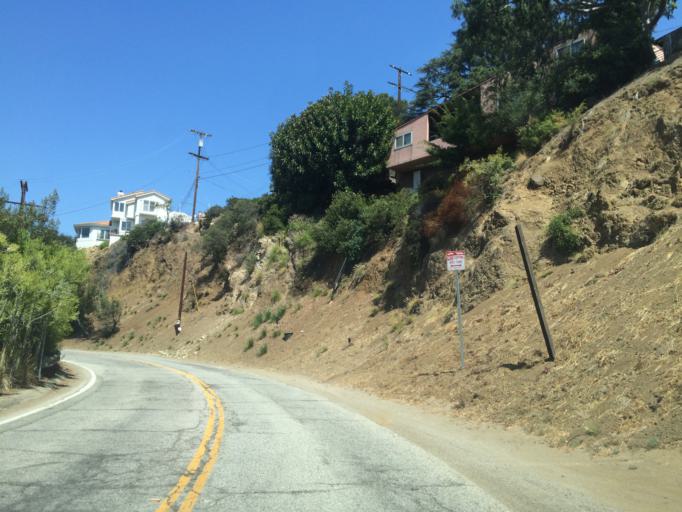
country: US
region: California
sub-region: Los Angeles County
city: Universal City
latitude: 34.1209
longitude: -118.3546
